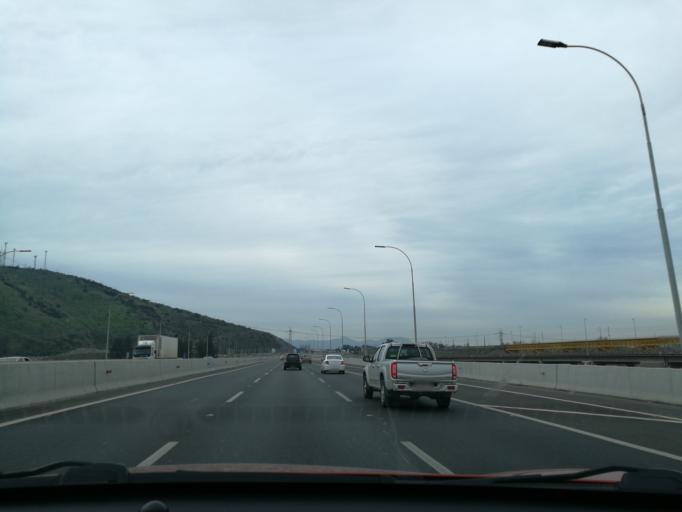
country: CL
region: Santiago Metropolitan
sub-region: Provincia de Maipo
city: Buin
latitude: -33.6926
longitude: -70.7244
